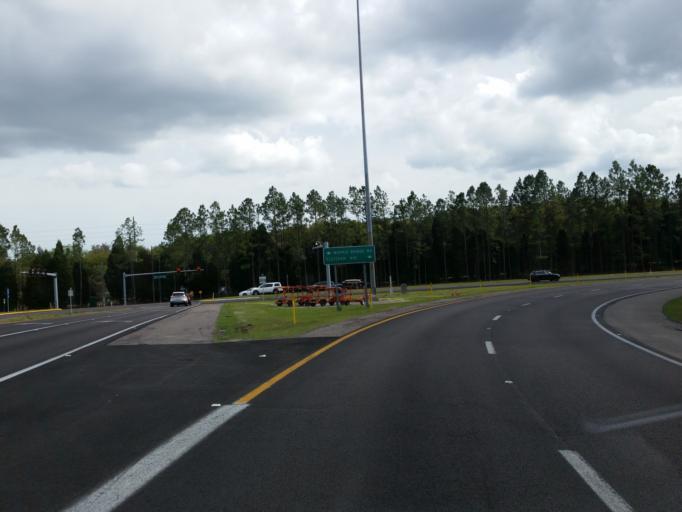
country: US
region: Florida
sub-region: Hillsborough County
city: Thonotosassa
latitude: 28.0728
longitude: -82.3499
